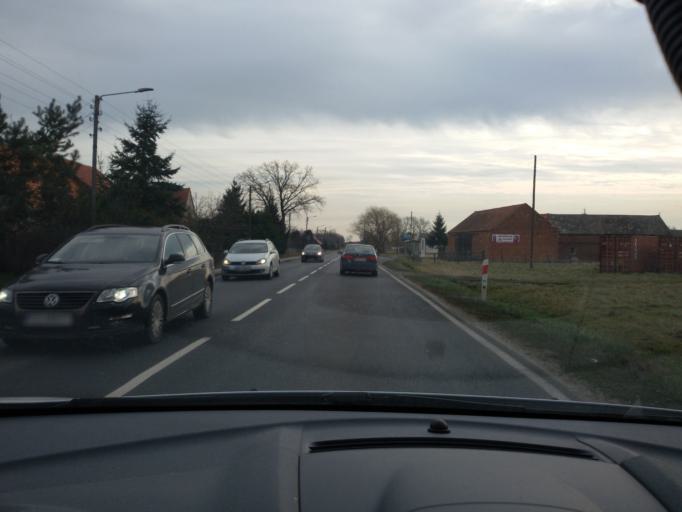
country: PL
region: Lubusz
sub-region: Powiat wschowski
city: Wschowa
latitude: 51.8179
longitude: 16.3739
